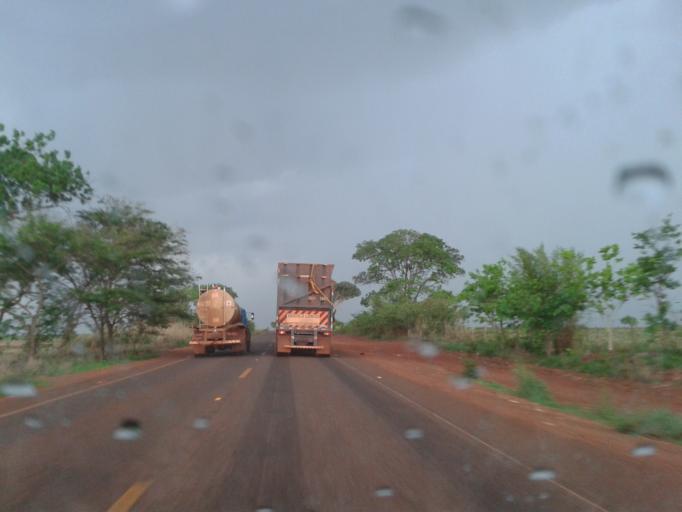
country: BR
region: Goias
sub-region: Quirinopolis
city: Quirinopolis
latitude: -18.5787
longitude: -50.4382
